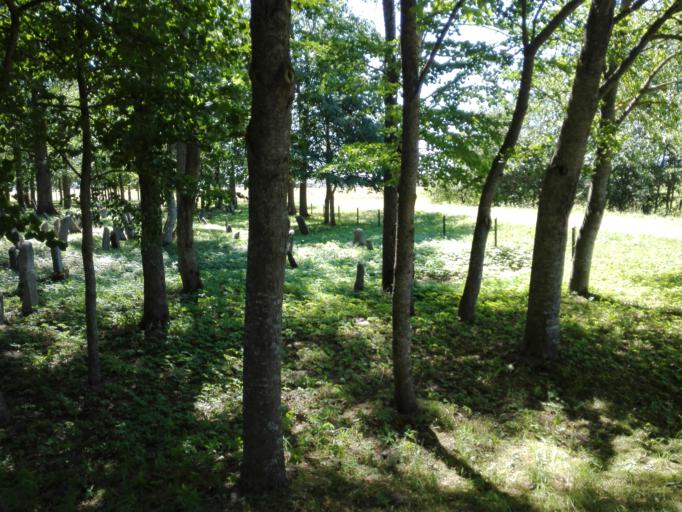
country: LT
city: Vabalninkas
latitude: 55.9802
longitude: 24.7603
